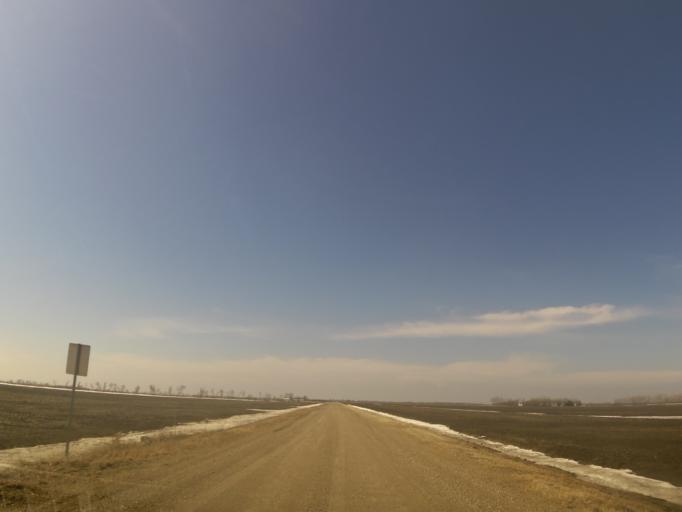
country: US
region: North Dakota
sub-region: Walsh County
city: Grafton
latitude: 48.4266
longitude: -97.2374
